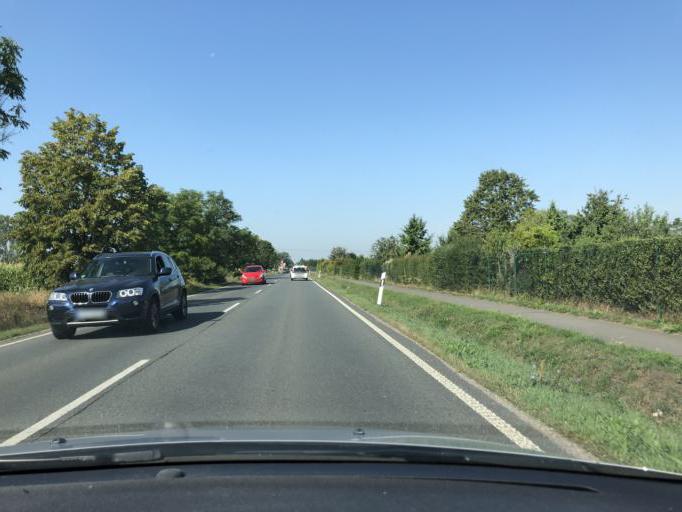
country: DE
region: Thuringia
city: Soemmerda
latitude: 51.1589
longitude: 11.1509
